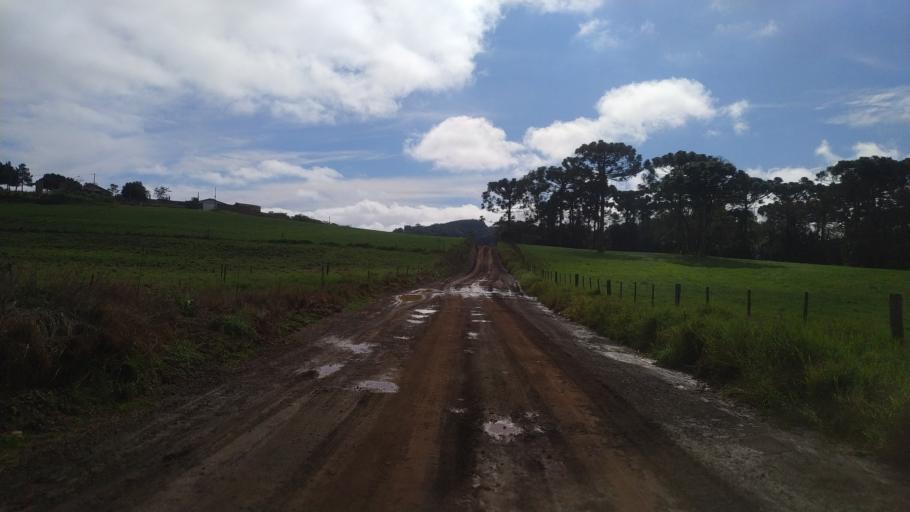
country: BR
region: Santa Catarina
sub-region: Chapeco
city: Chapeco
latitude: -27.1512
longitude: -52.5951
